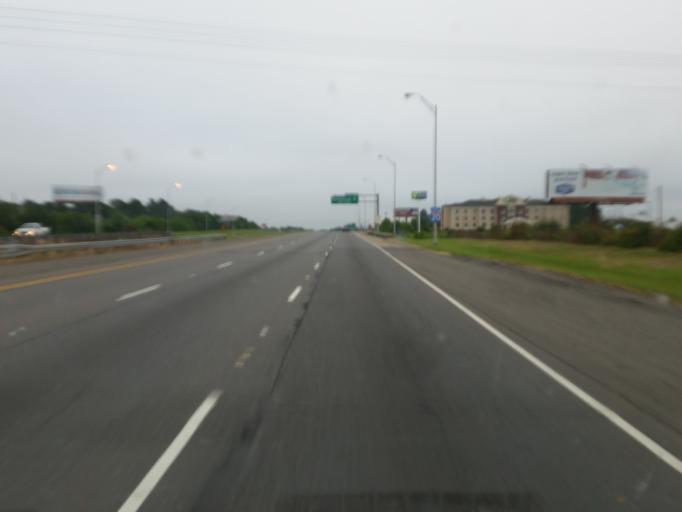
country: US
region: Louisiana
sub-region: Caddo Parish
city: Shreveport
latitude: 32.4591
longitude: -93.8350
